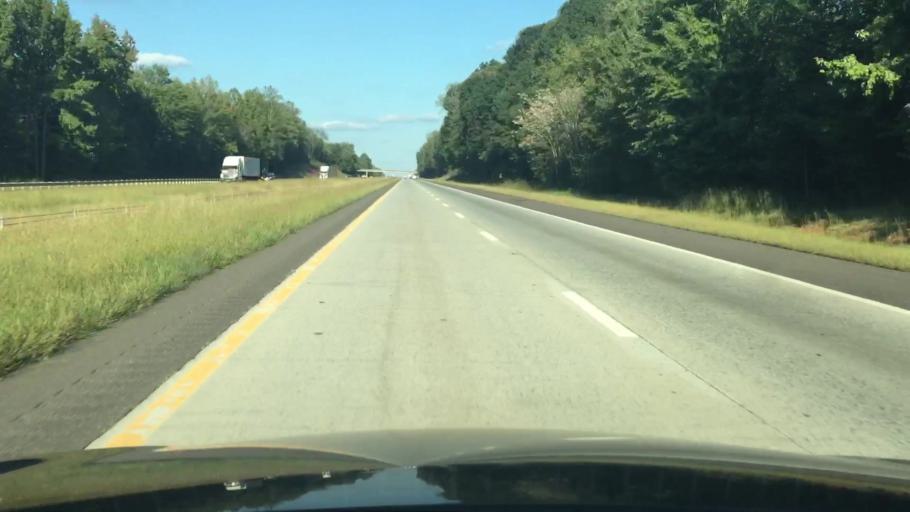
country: US
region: North Carolina
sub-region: Davie County
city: Mocksville
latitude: 35.8830
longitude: -80.6787
